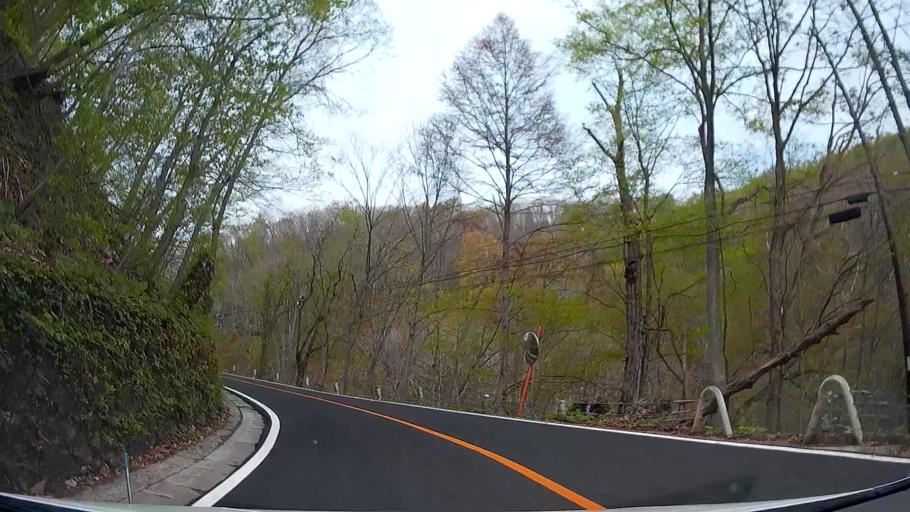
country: JP
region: Akita
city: Hanawa
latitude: 40.3874
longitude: 140.8845
